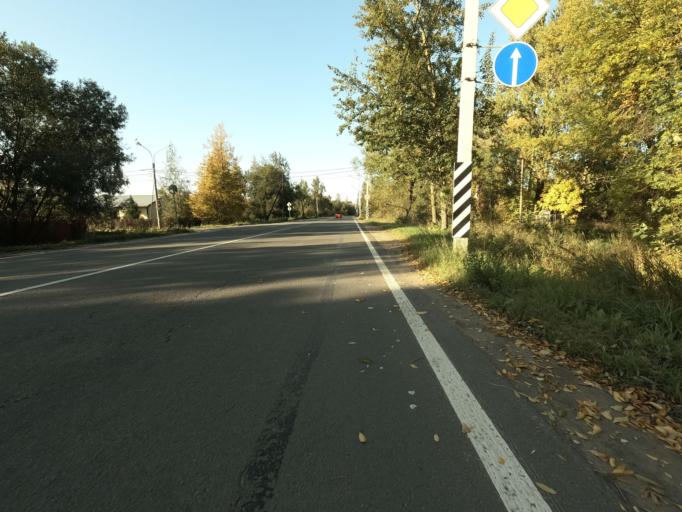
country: RU
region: St.-Petersburg
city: Kolpino
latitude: 59.7524
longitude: 30.6158
